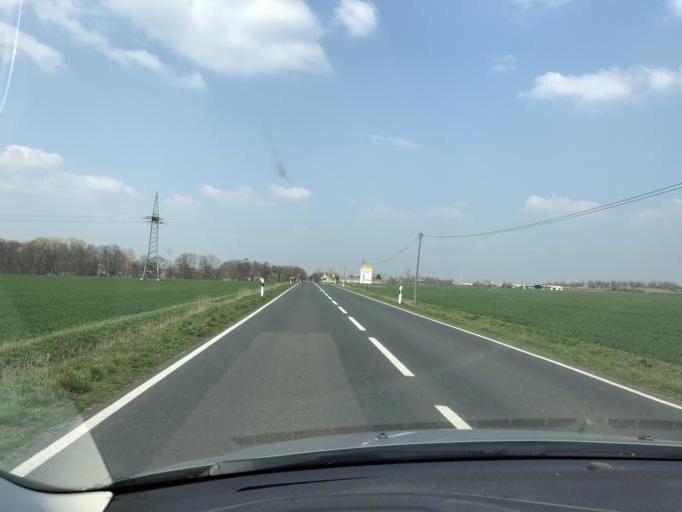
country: DE
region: Saxony-Anhalt
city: Landsberg
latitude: 51.5775
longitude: 12.1433
